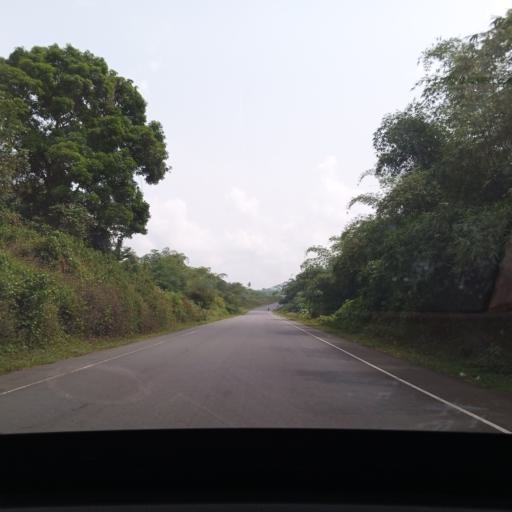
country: LR
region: Margibi
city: Kakata
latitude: 6.2536
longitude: -10.3089
